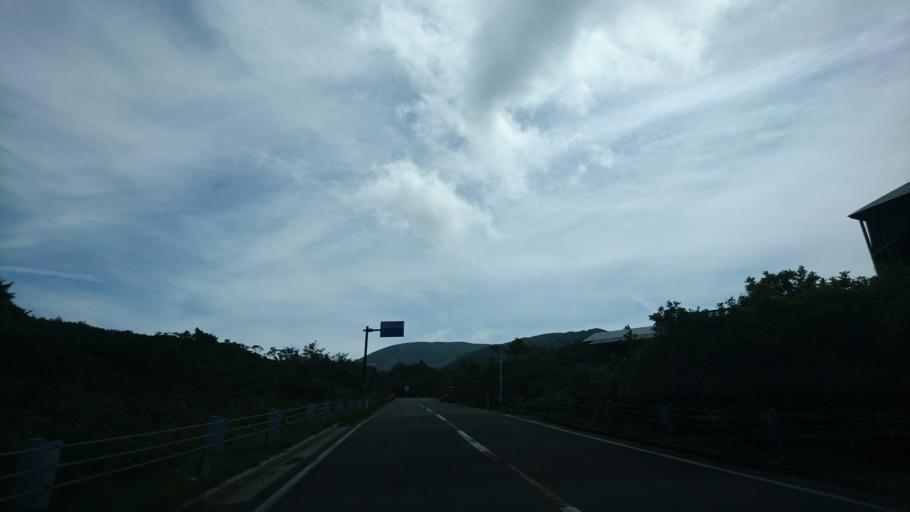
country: JP
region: Akita
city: Yuzawa
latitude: 38.9808
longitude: 140.7673
